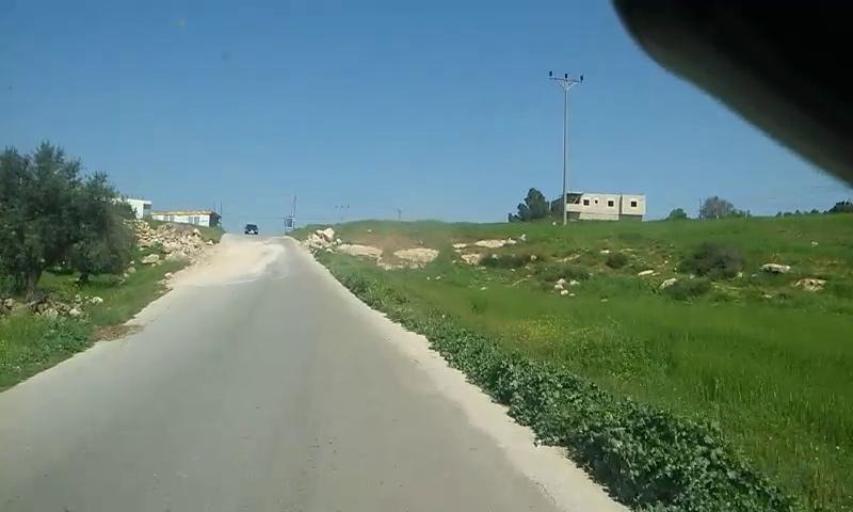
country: PS
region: West Bank
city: Al Majd
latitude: 31.4753
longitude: 34.9505
